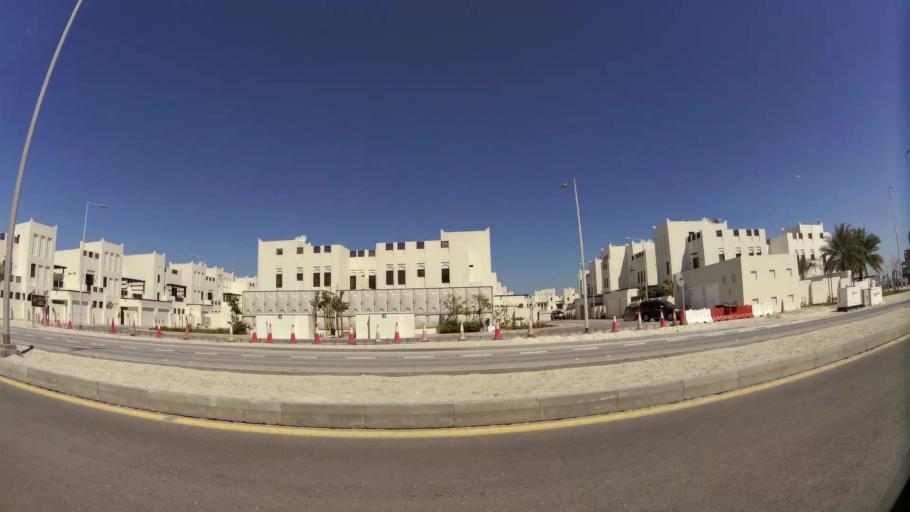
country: BH
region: Muharraq
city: Al Muharraq
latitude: 26.2996
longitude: 50.6368
